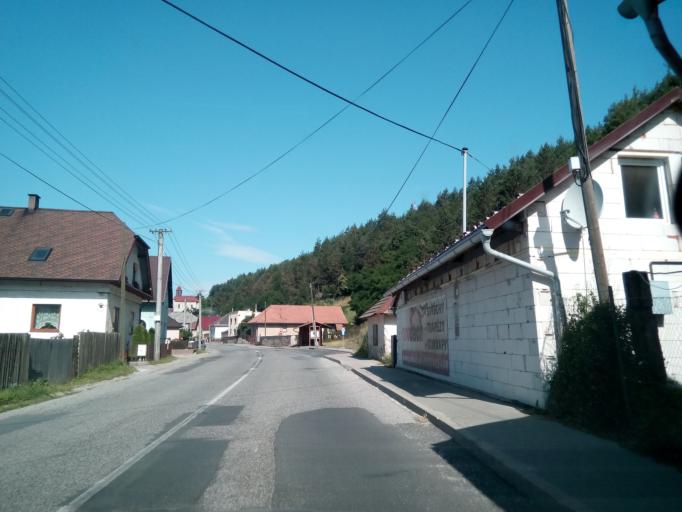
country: SK
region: Kosicky
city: Krompachy
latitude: 48.9280
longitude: 20.8547
